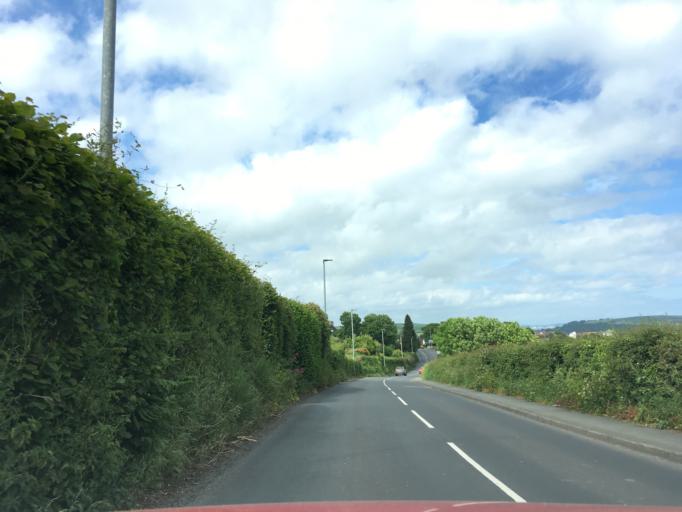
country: GB
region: England
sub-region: Devon
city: Dartmouth
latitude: 50.3478
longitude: -3.5952
